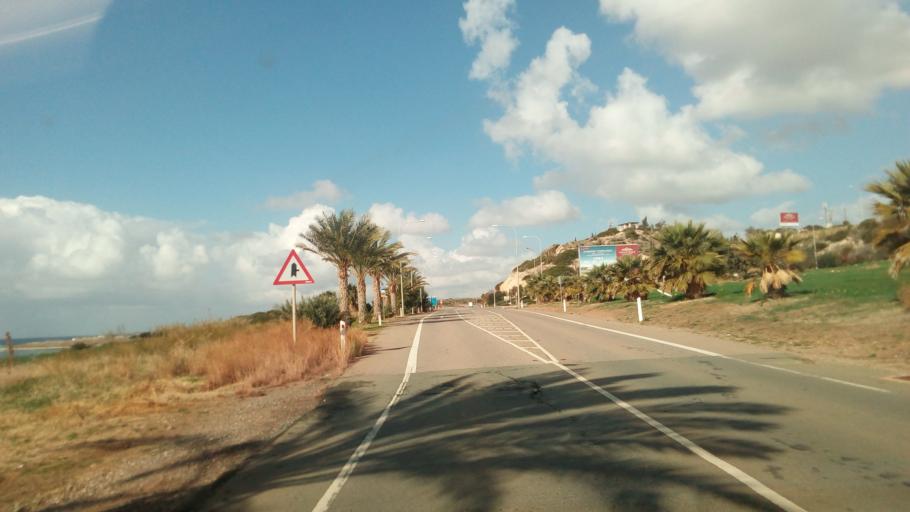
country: CY
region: Limassol
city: Pissouri
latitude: 34.6859
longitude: 32.5849
